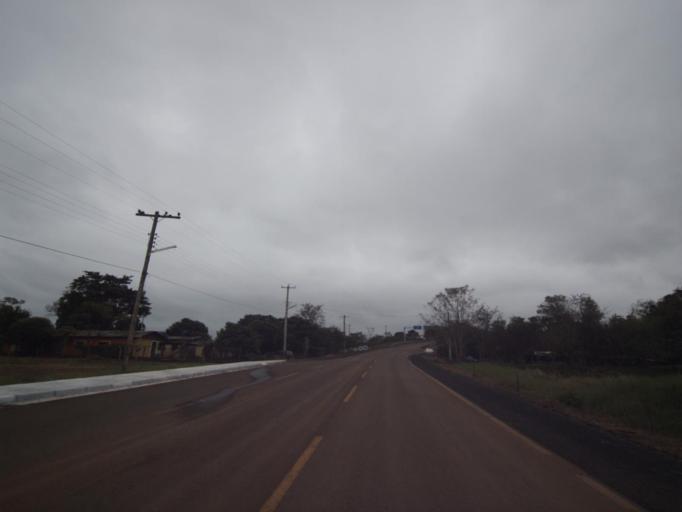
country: AR
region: Misiones
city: El Soberbio
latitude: -27.2911
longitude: -54.1900
